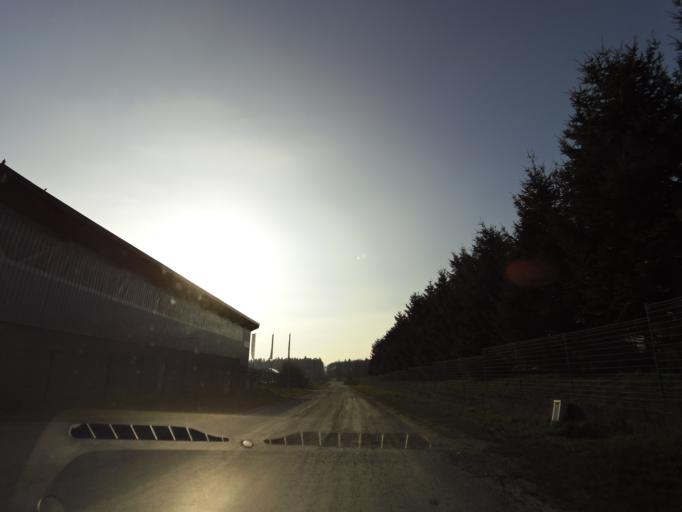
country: FR
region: Brittany
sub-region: Departement d'Ille-et-Vilaine
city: Corps-Nuds
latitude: 47.9860
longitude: -1.5864
